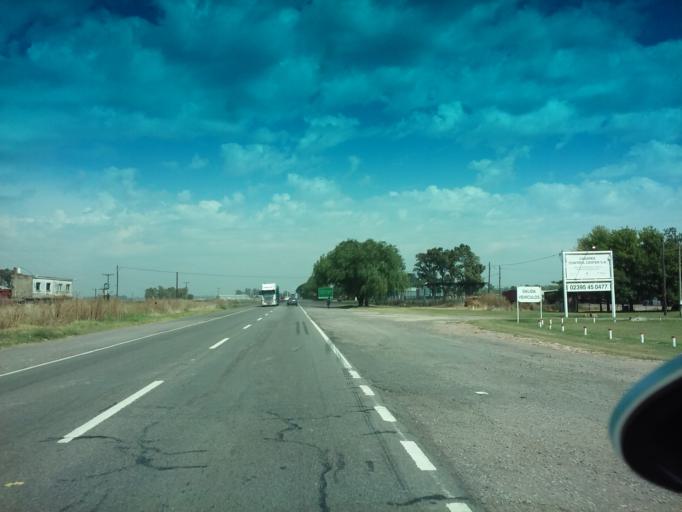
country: AR
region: Buenos Aires
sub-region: Partido de Carlos Casares
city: Carlos Casares
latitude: -35.6329
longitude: -61.3447
